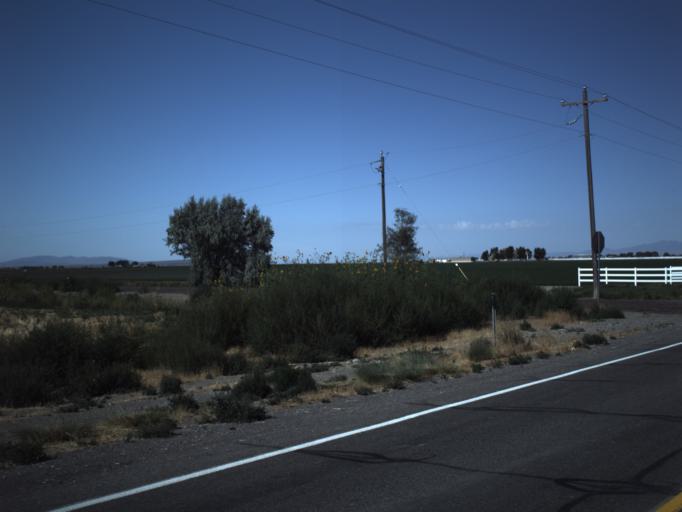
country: US
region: Utah
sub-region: Millard County
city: Delta
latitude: 39.3305
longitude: -112.6249
